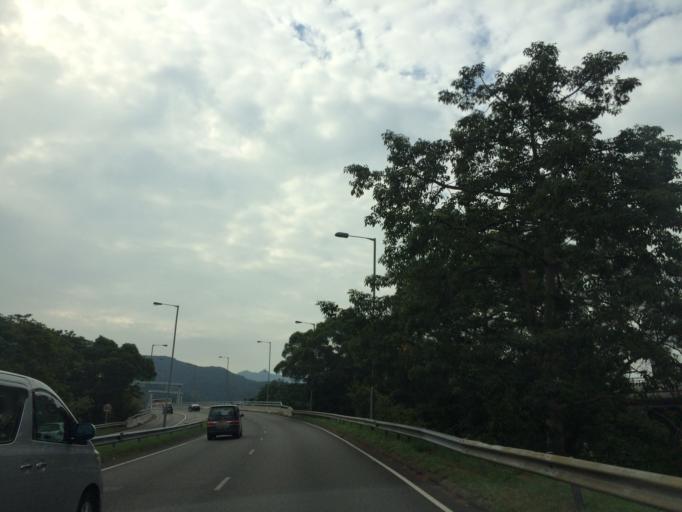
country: HK
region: Sha Tin
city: Sha Tin
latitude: 22.4118
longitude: 114.2127
